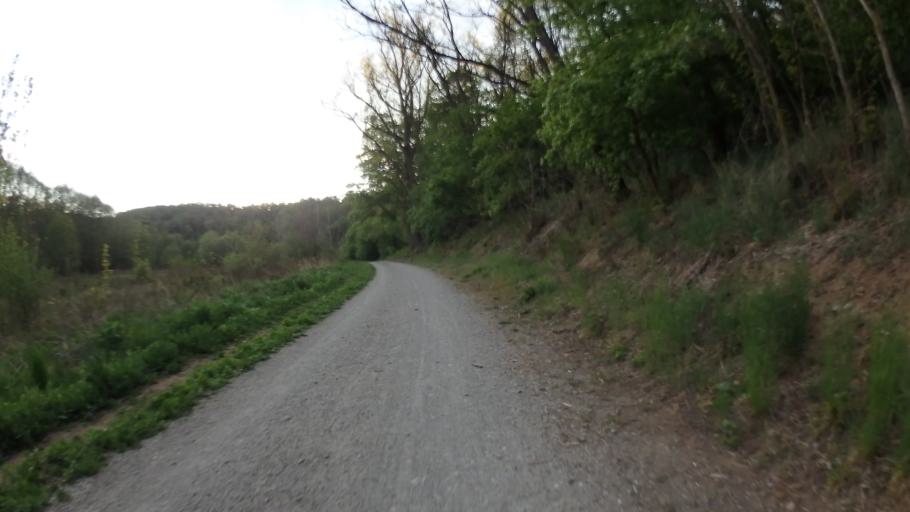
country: CZ
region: South Moravian
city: Strelice
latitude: 49.1437
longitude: 16.4816
